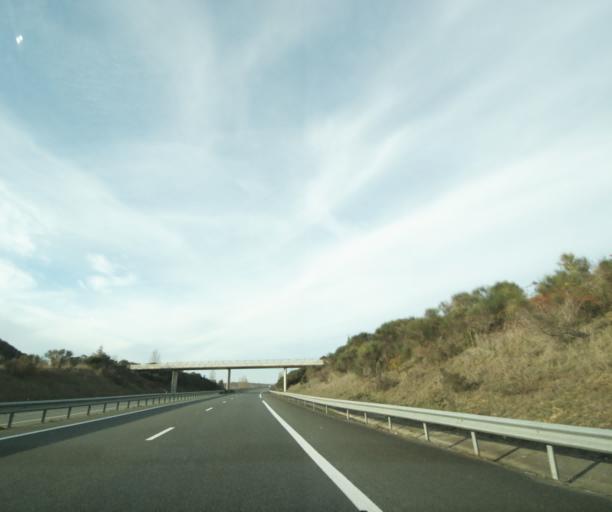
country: FR
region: Midi-Pyrenees
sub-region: Departement du Gers
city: Aubiet
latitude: 43.6472
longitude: 0.7973
